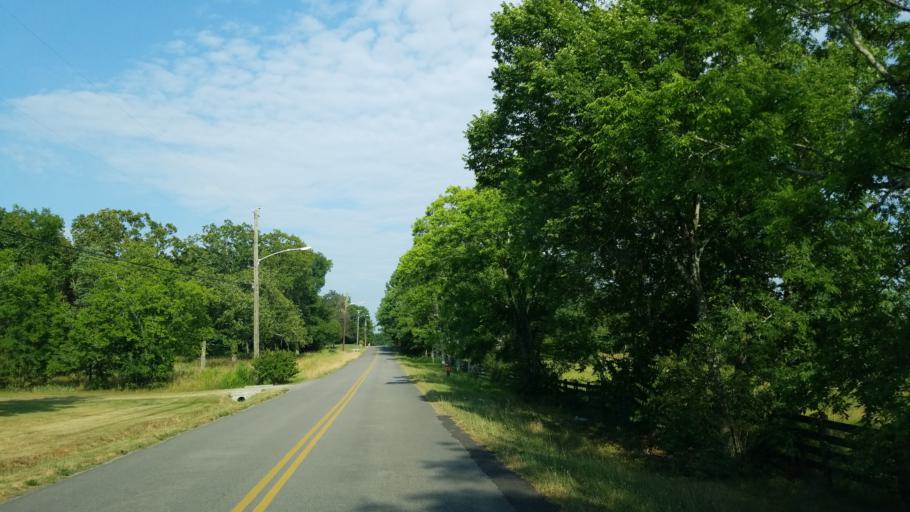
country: US
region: Tennessee
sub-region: Rutherford County
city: La Vergne
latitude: 36.0378
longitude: -86.5904
